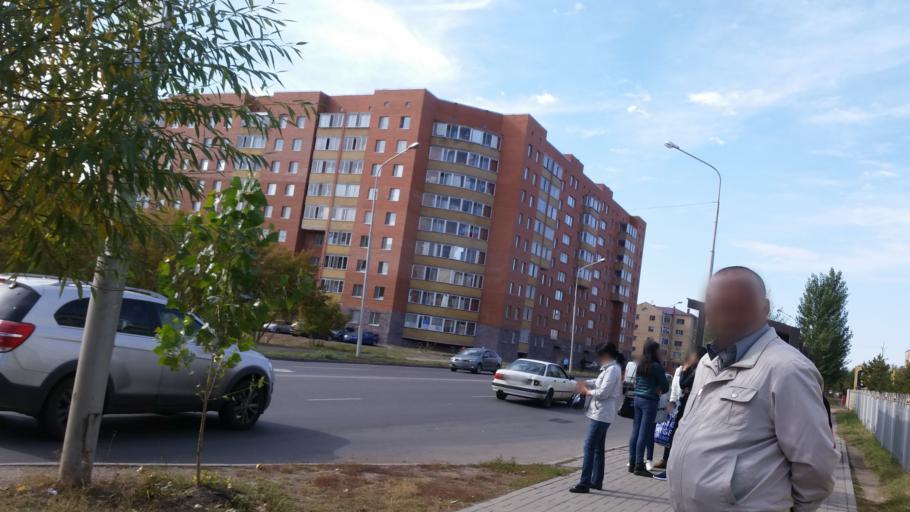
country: KZ
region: Astana Qalasy
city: Astana
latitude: 51.1598
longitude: 71.4907
